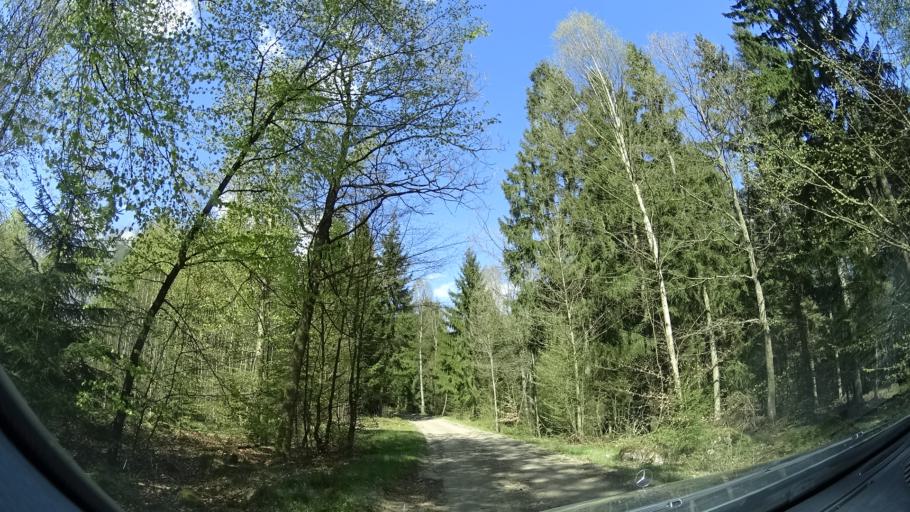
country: SE
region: Skane
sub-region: Hassleholms Kommun
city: Tormestorp
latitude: 56.0945
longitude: 13.6937
